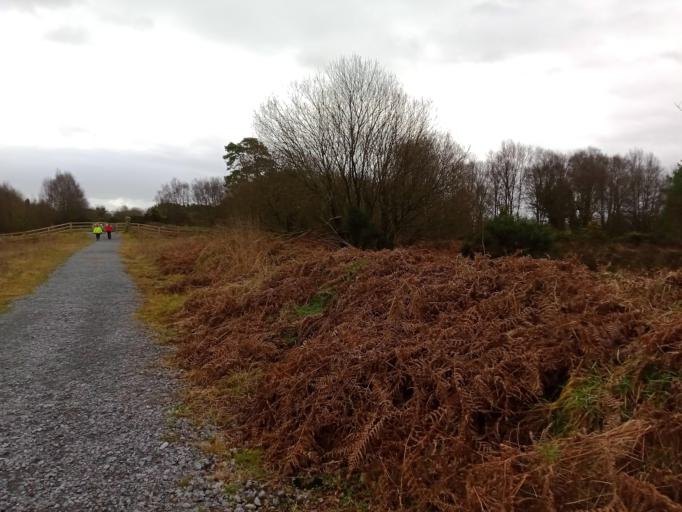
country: IE
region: Munster
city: Thurles
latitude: 52.5939
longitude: -7.7425
